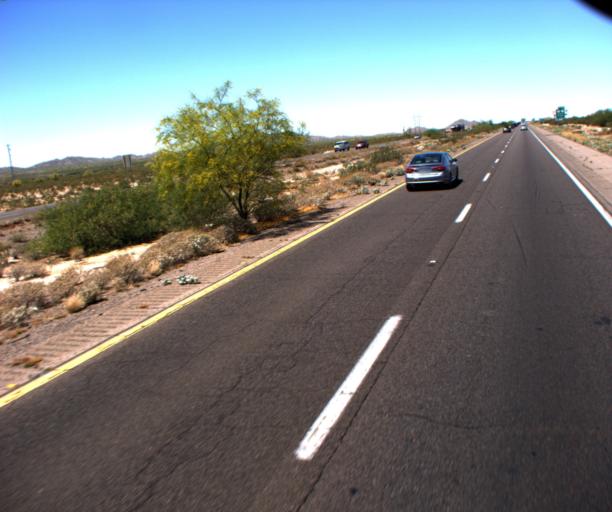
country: US
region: Arizona
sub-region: Pinal County
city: Sacaton
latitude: 32.9922
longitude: -111.7440
